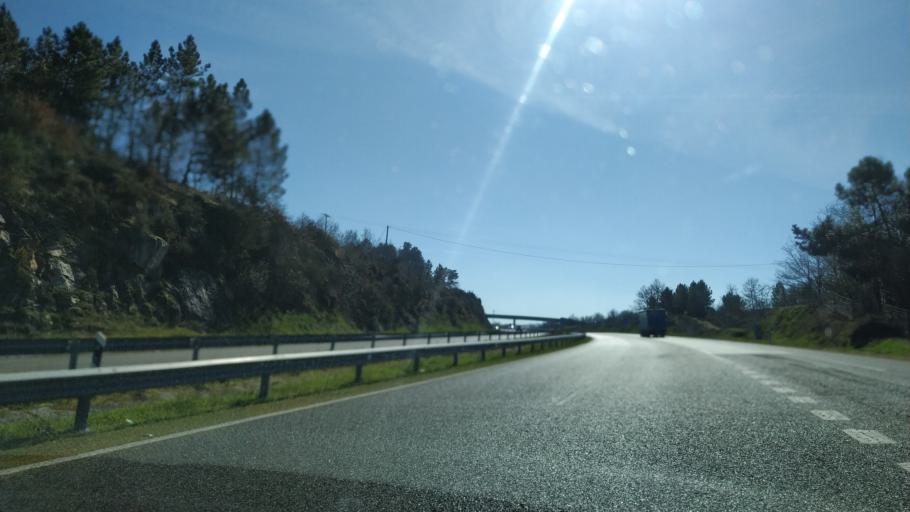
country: ES
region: Galicia
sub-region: Provincia de Ourense
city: Taboadela
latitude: 42.2703
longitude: -7.8716
